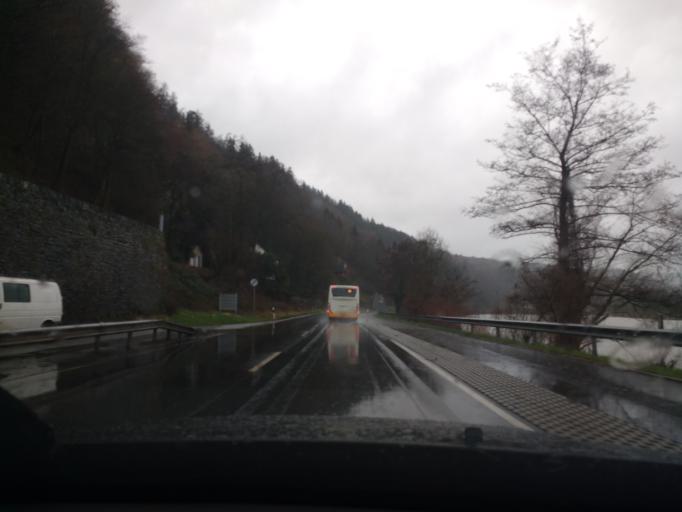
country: DE
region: Rheinland-Pfalz
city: Traben-Trarbach
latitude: 49.9512
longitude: 7.1075
